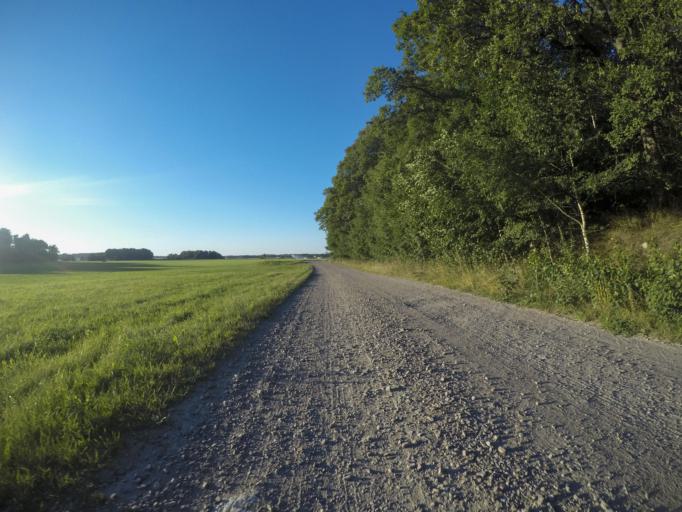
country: SE
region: Vaestmanland
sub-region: Vasteras
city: Vasteras
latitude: 59.5726
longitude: 16.6523
